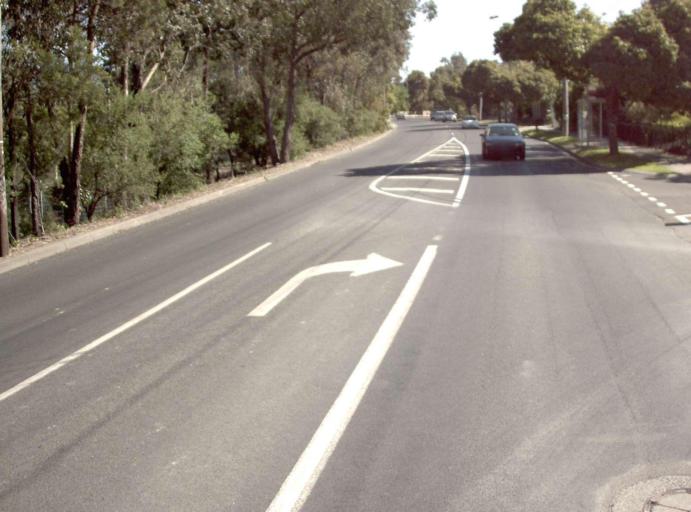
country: AU
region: Victoria
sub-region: Maroondah
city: Croydon South
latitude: -37.7980
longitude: 145.2757
